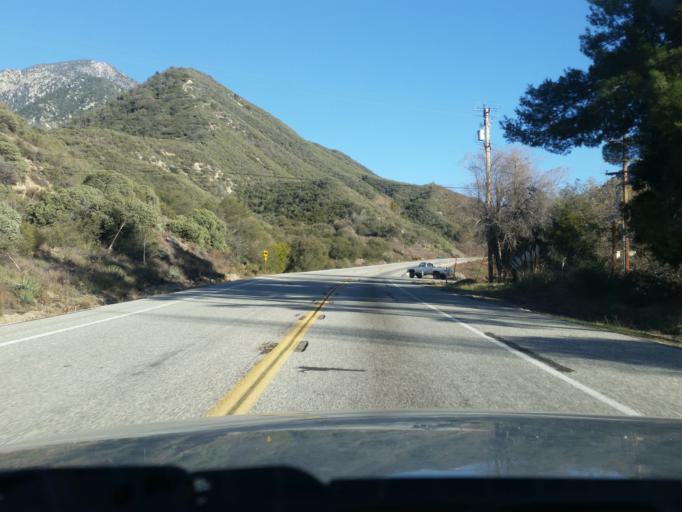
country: US
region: California
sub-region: San Bernardino County
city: Yucaipa
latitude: 34.1025
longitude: -116.9966
